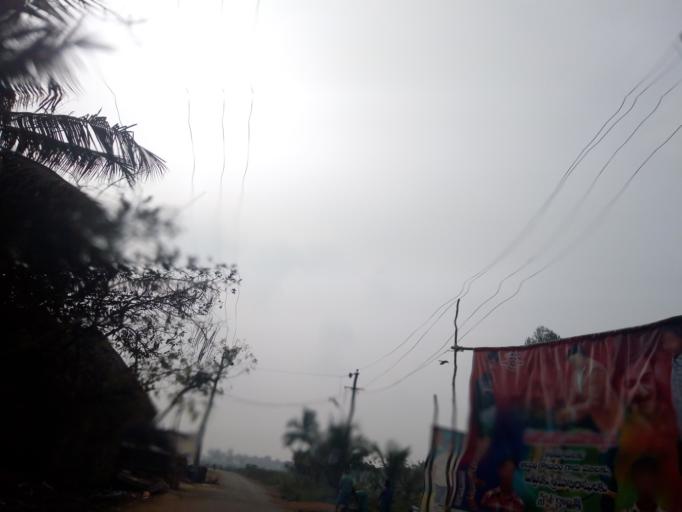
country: IN
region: Andhra Pradesh
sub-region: West Godavari
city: Tadepallegudem
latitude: 16.8352
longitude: 81.3486
